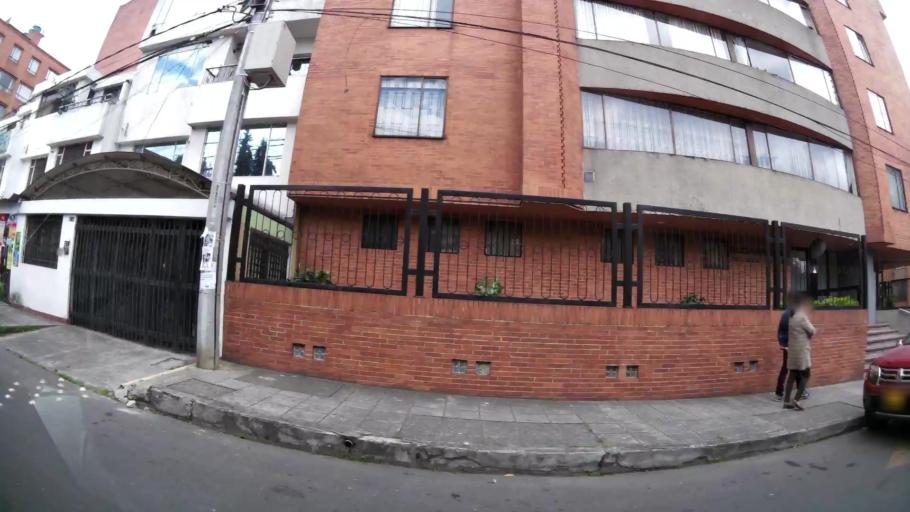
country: CO
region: Bogota D.C.
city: Bogota
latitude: 4.6345
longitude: -74.0973
